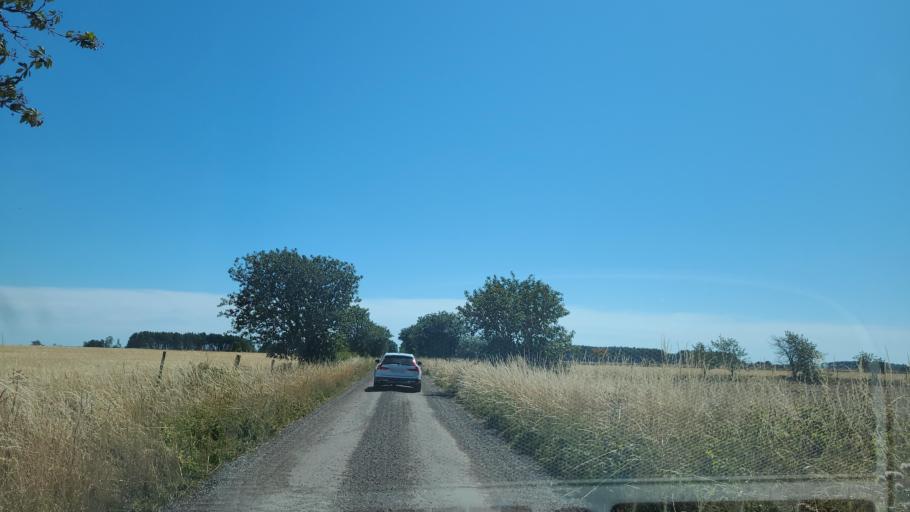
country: SE
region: Kalmar
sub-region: Morbylanga Kommun
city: Sodra Sandby
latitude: 56.7101
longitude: 16.7227
